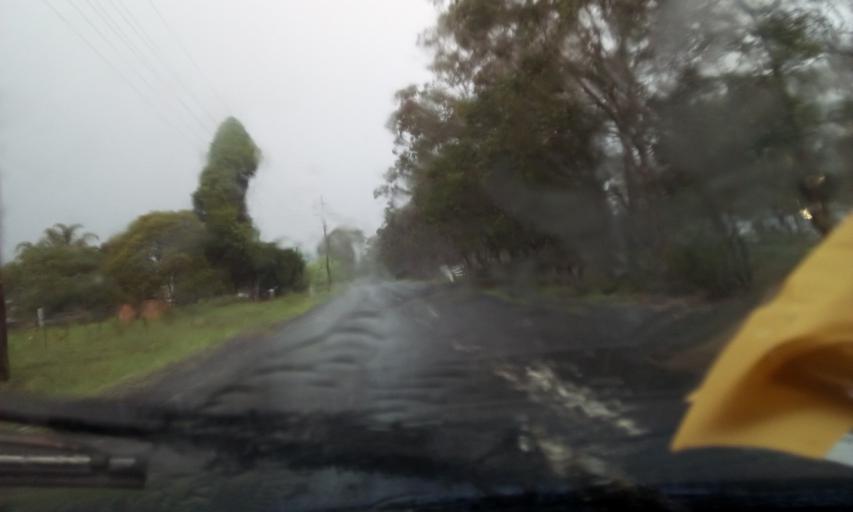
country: AU
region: New South Wales
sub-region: Wollondilly
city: Douglas Park
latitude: -34.2321
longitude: 150.7288
